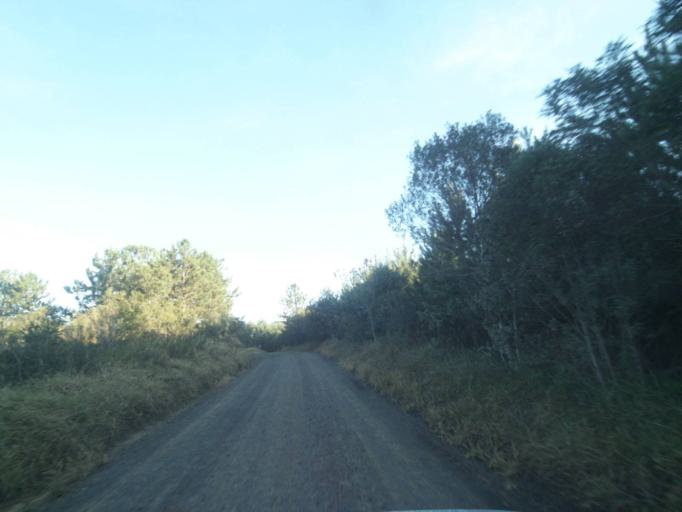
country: BR
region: Parana
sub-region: Telemaco Borba
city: Telemaco Borba
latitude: -24.4284
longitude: -50.5970
